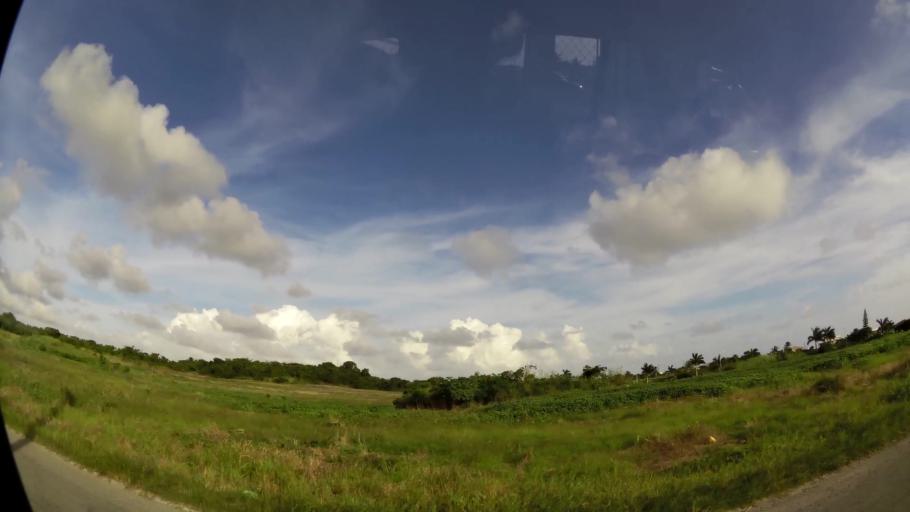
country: BB
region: Christ Church
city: Oistins
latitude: 13.0801
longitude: -59.5573
